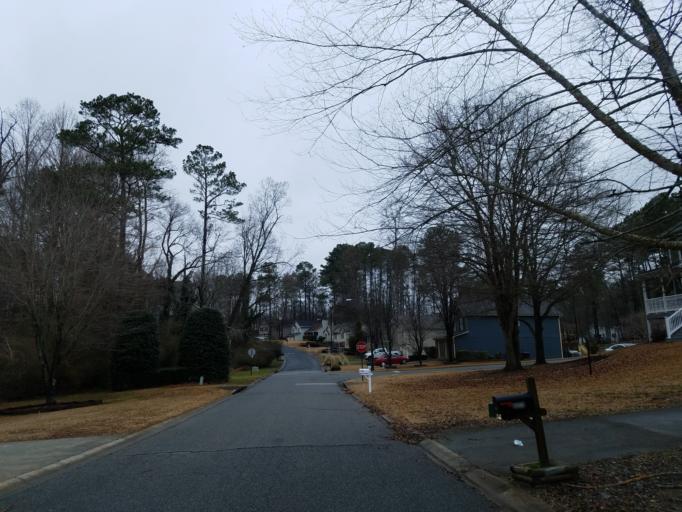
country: US
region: Georgia
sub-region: Cobb County
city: Acworth
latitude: 34.0731
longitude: -84.6629
